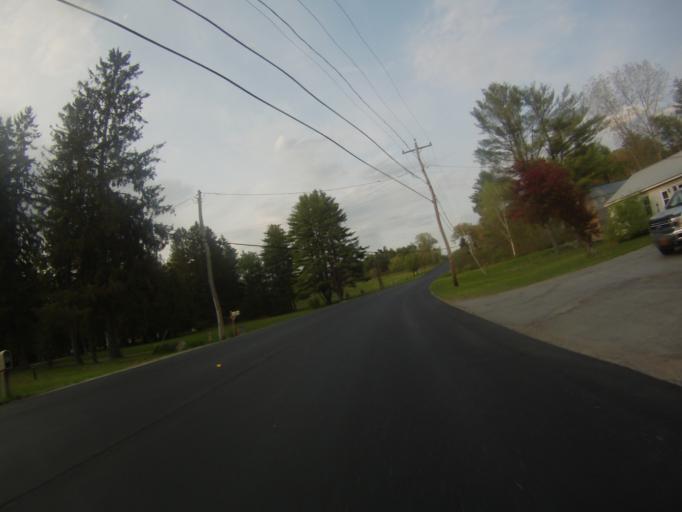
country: US
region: New York
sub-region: Essex County
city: Ticonderoga
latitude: 43.8104
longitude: -73.4885
